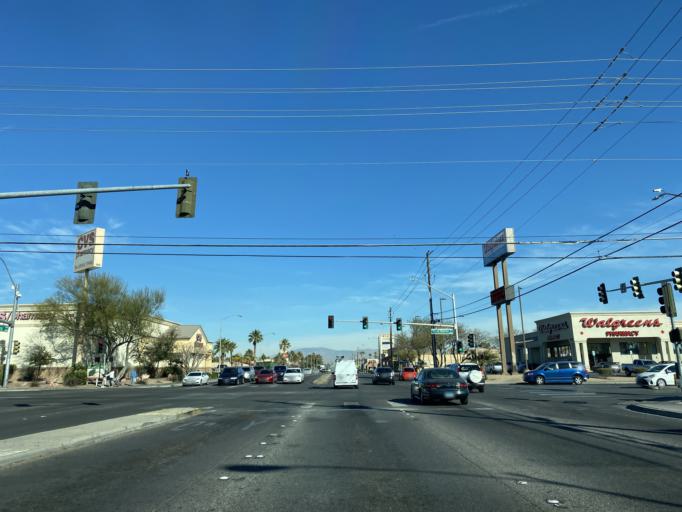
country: US
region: Nevada
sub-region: Clark County
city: Spring Valley
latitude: 36.1252
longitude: -115.2249
